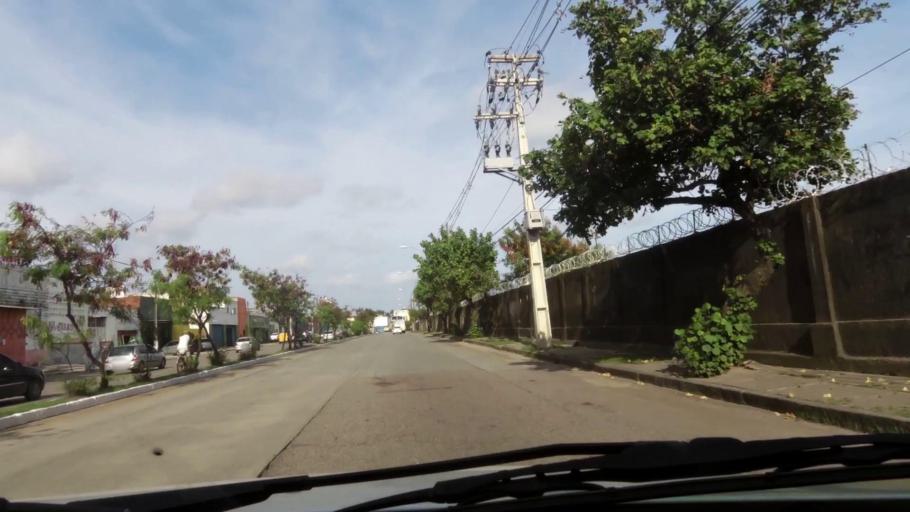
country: BR
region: Pernambuco
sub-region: Recife
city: Recife
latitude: -8.0735
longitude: -34.8857
